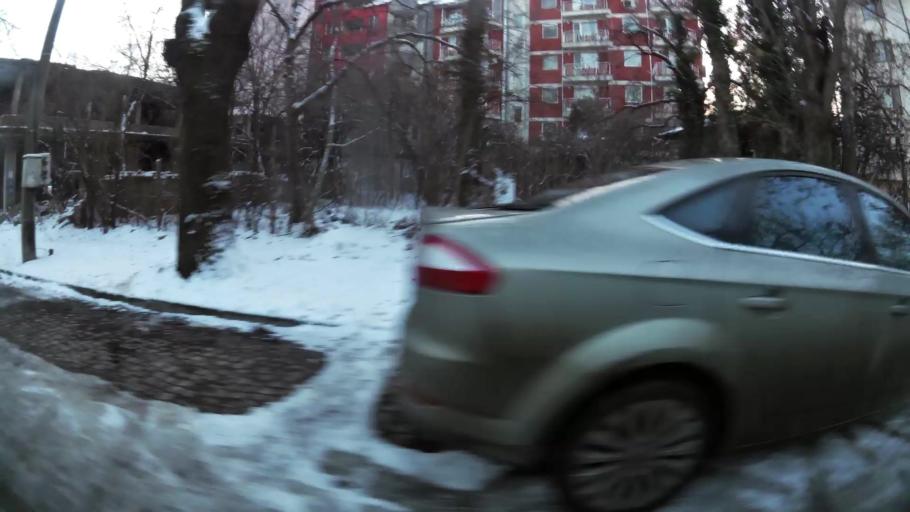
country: BG
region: Sofia-Capital
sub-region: Stolichna Obshtina
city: Sofia
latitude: 42.6823
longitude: 23.3729
